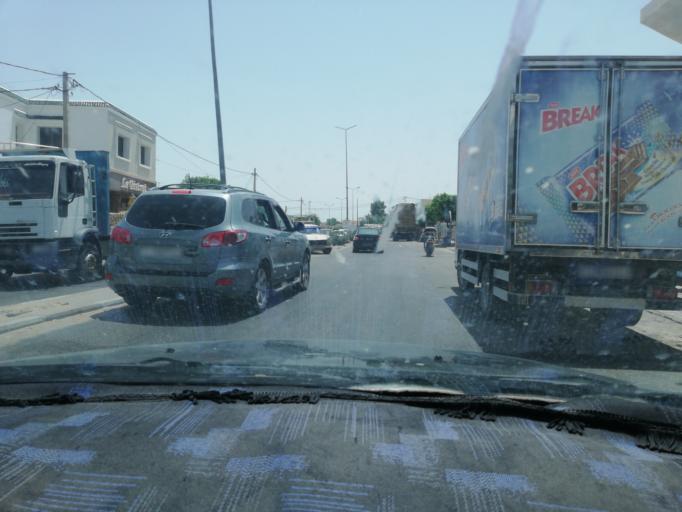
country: TN
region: Qabis
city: Gabes
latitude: 33.6211
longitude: 10.2831
